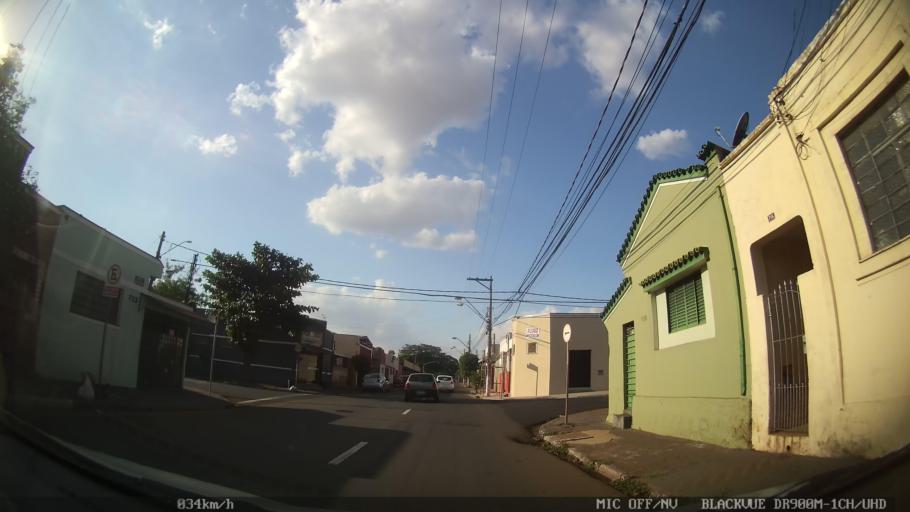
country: BR
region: Sao Paulo
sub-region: Ribeirao Preto
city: Ribeirao Preto
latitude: -21.1602
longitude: -47.8085
